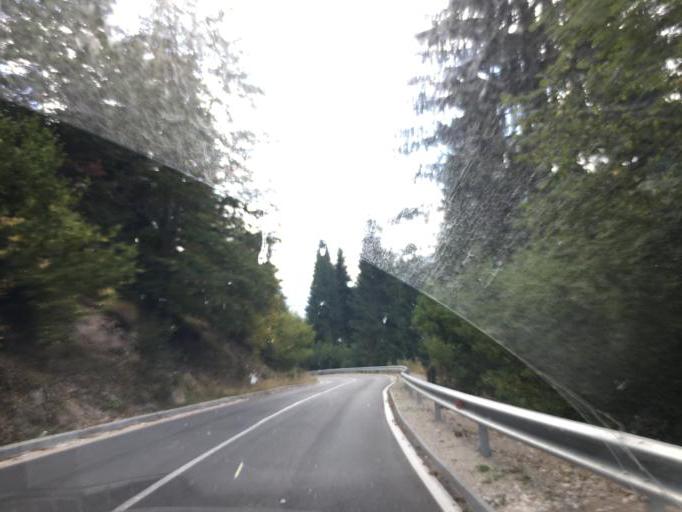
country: BG
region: Pazardzhik
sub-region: Obshtina Batak
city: Batak
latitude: 41.8980
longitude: 24.3164
